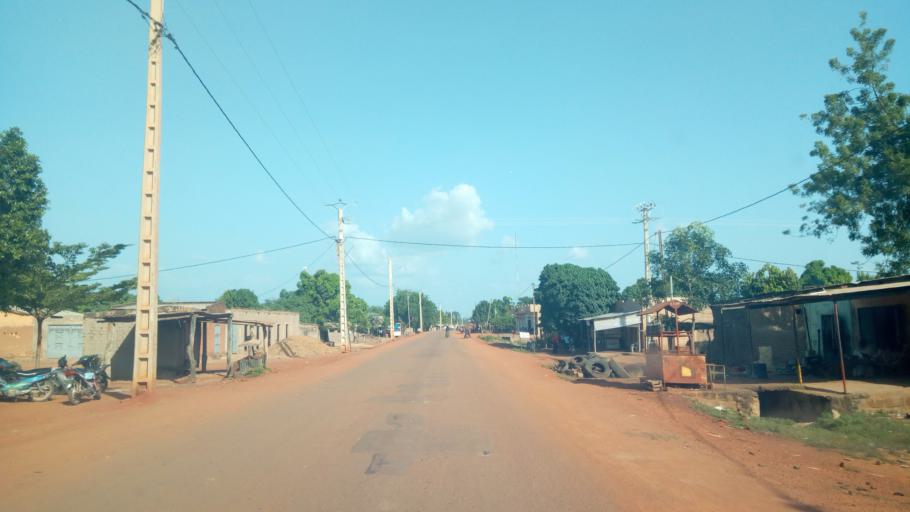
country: ML
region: Sikasso
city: Yorosso
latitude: 12.1840
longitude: -4.8079
